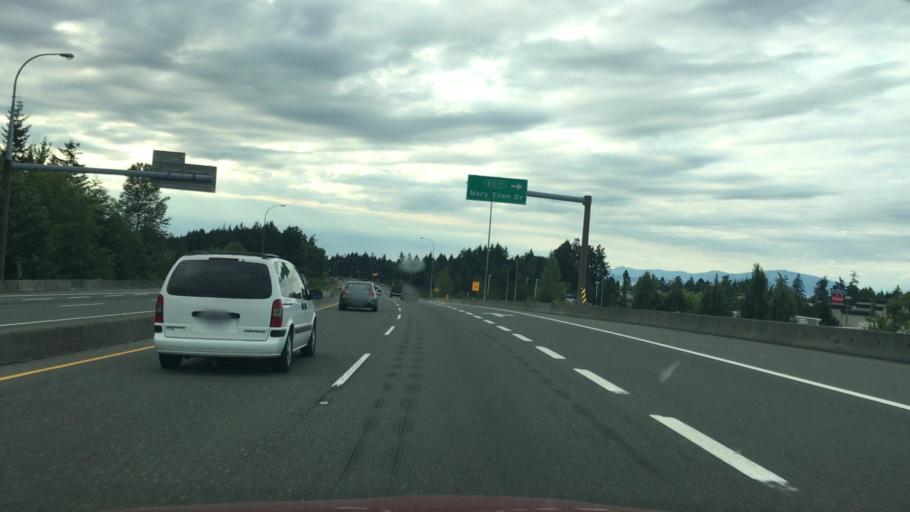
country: CA
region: British Columbia
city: Nanaimo
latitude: 49.2363
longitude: -124.0540
